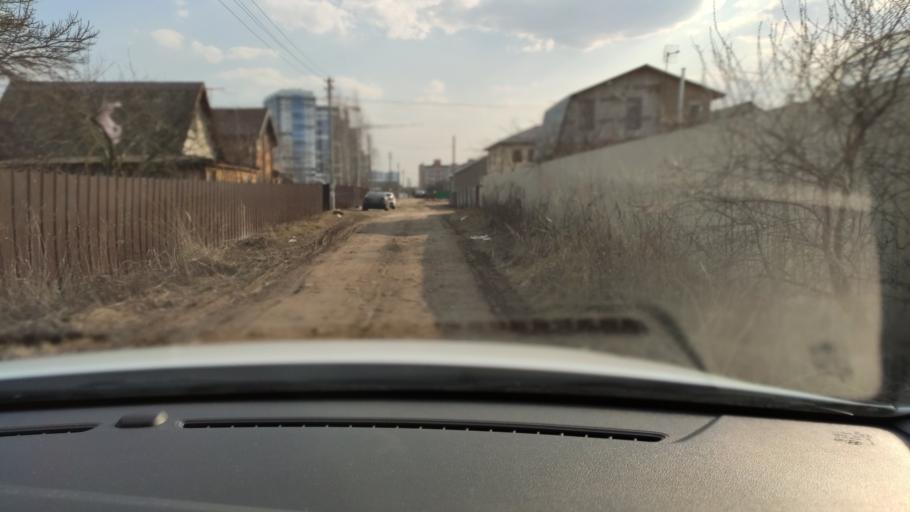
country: RU
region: Tatarstan
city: Stolbishchi
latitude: 55.6936
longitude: 49.2018
